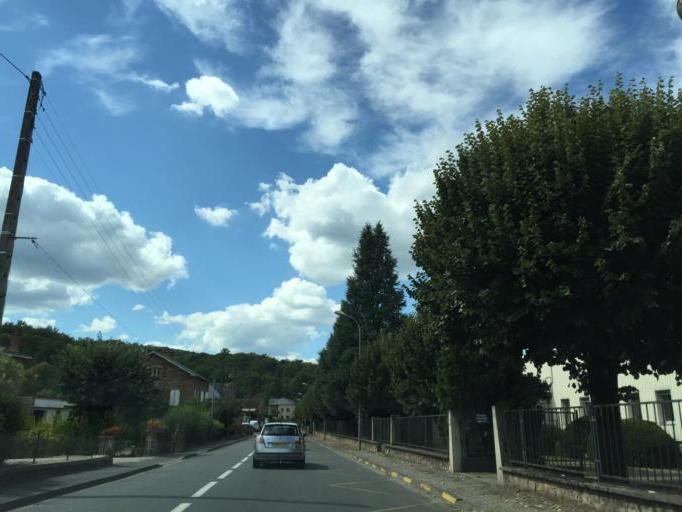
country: FR
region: Midi-Pyrenees
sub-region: Departement de l'Aveyron
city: Marcillac-Vallon
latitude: 44.4754
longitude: 2.4586
